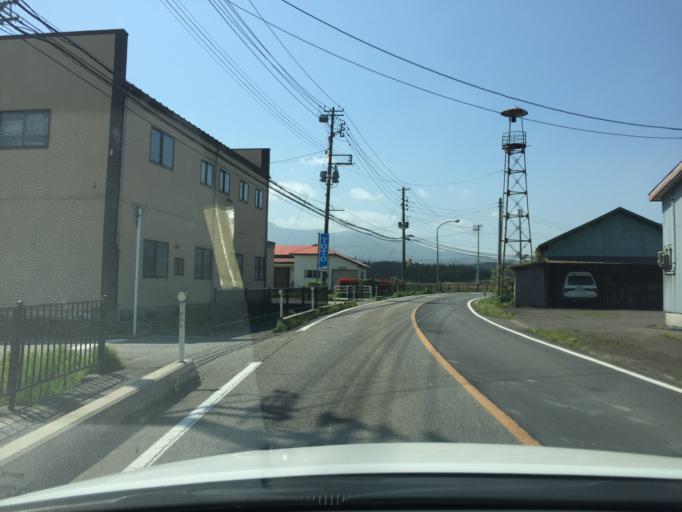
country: JP
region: Niigata
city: Muramatsu
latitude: 37.6842
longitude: 139.1522
